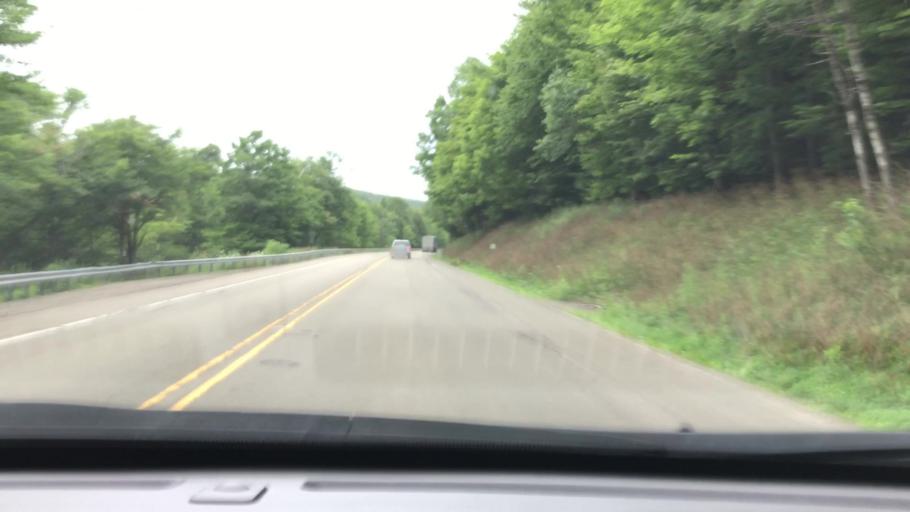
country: US
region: Pennsylvania
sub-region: McKean County
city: Kane
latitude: 41.6639
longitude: -78.6817
